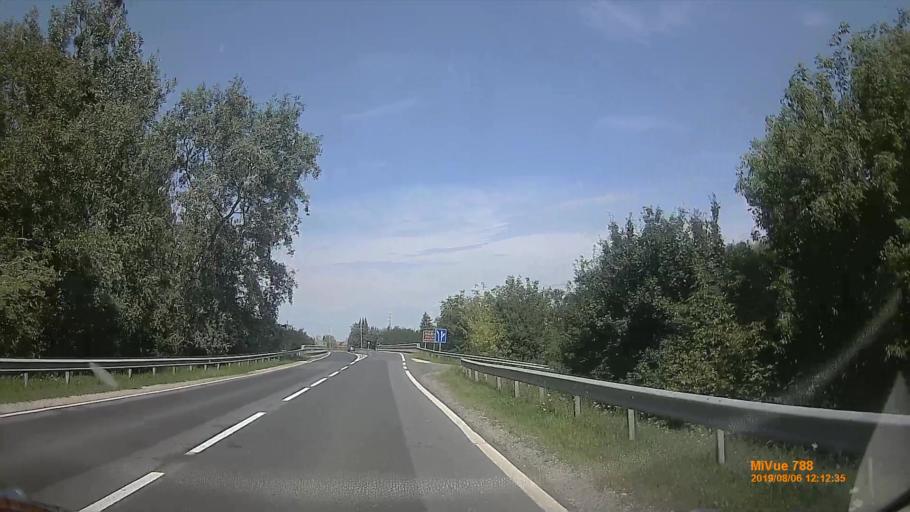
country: HU
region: Vas
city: Vasvar
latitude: 47.1258
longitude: 16.8489
